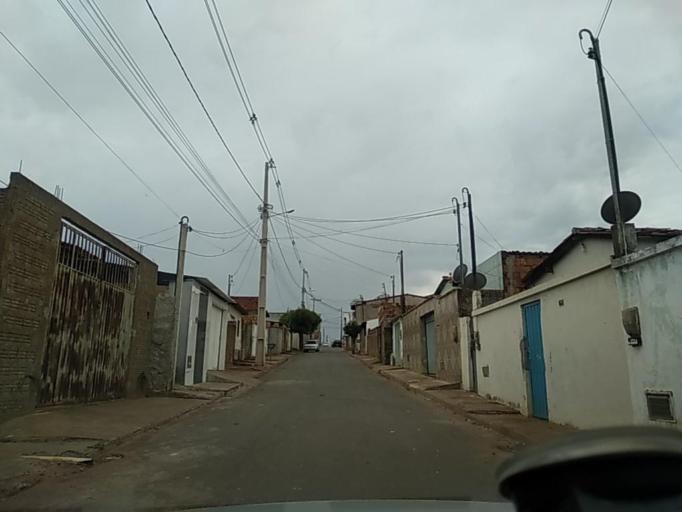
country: BR
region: Bahia
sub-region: Caetite
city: Caetite
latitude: -14.0584
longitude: -42.4796
